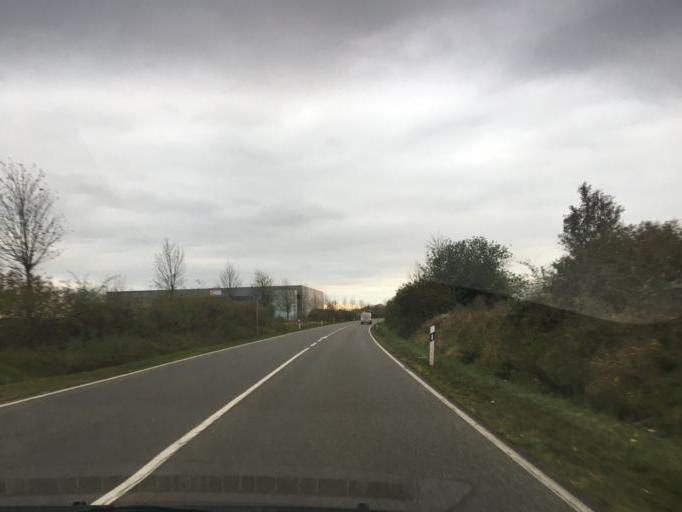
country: DE
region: North Rhine-Westphalia
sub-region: Regierungsbezirk Koln
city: Erftstadt
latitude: 50.7939
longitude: 6.7801
